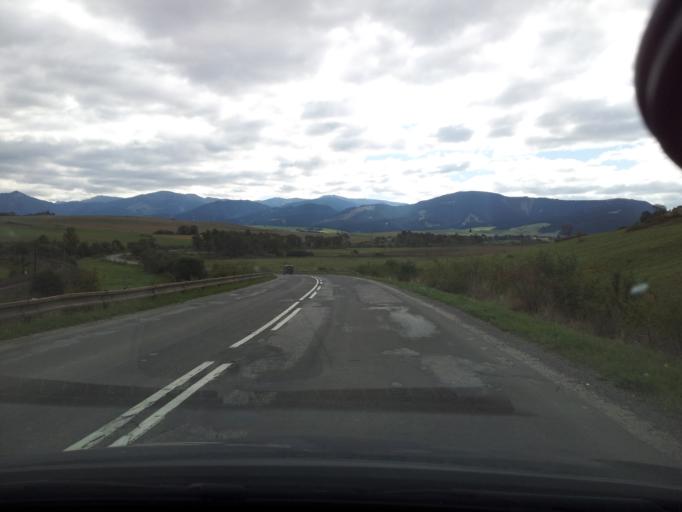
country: SK
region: Zilinsky
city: Ruzomberok
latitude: 49.0886
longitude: 19.4348
